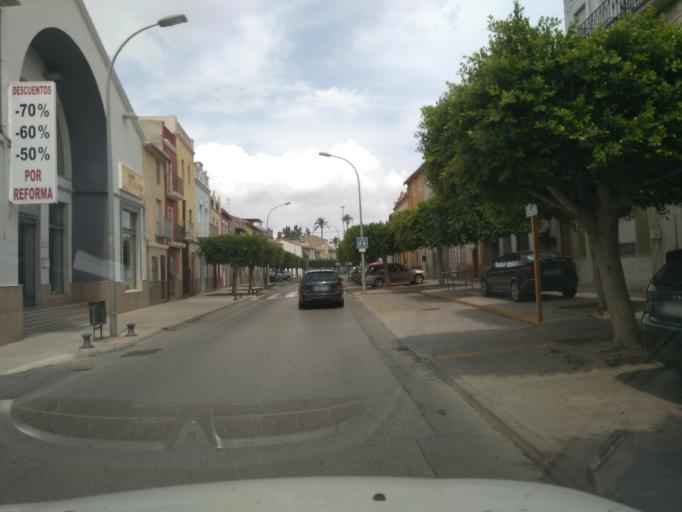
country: ES
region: Valencia
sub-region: Provincia de Valencia
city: Carcaixent
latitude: 39.1275
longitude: -0.4495
